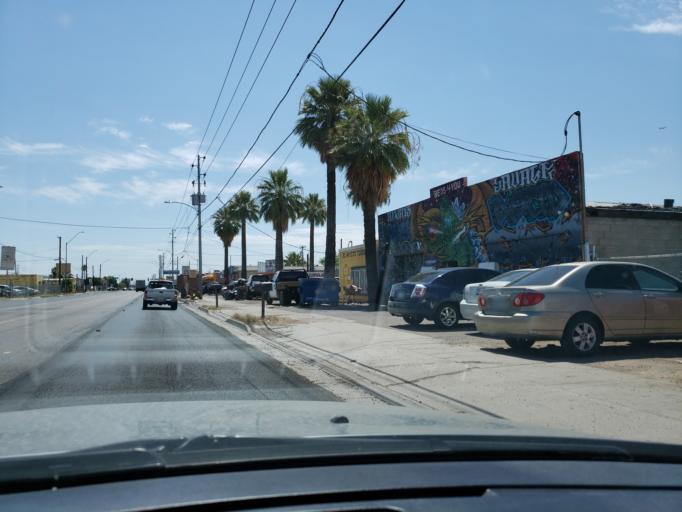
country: US
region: Arizona
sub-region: Maricopa County
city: Phoenix
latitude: 33.4368
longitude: -112.1208
